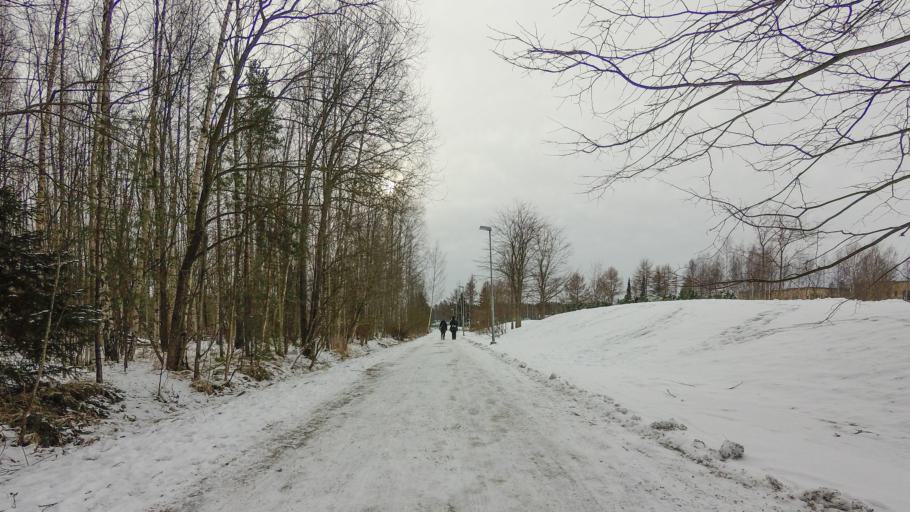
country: FI
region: Uusimaa
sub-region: Helsinki
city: Vantaa
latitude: 60.1773
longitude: 25.0564
